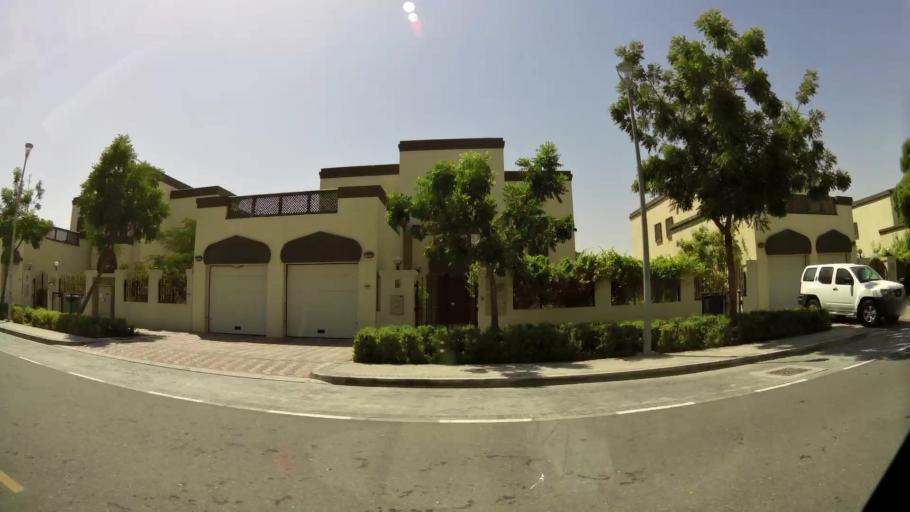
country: AE
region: Dubai
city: Dubai
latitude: 25.0475
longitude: 55.1564
